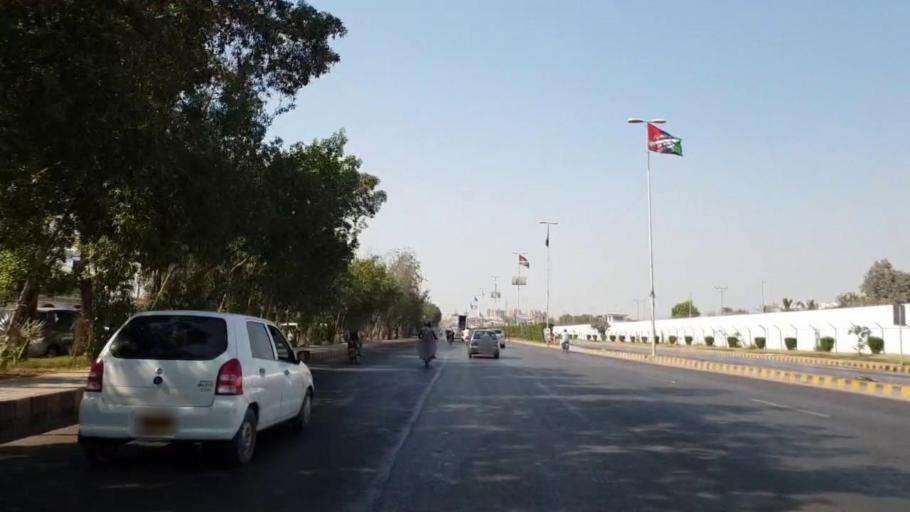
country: PK
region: Sindh
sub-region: Karachi District
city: Karachi
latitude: 24.8770
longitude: 67.0949
